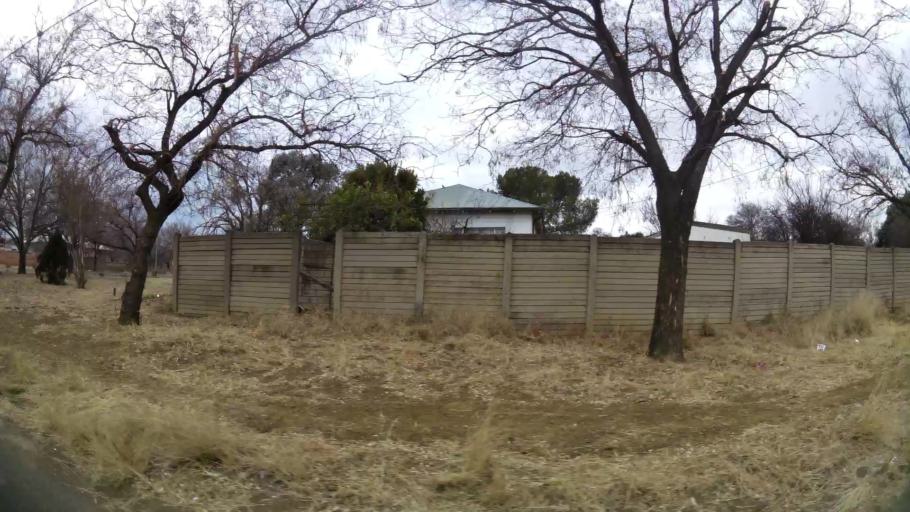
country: ZA
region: Orange Free State
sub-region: Fezile Dabi District Municipality
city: Kroonstad
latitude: -27.6810
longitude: 27.2309
